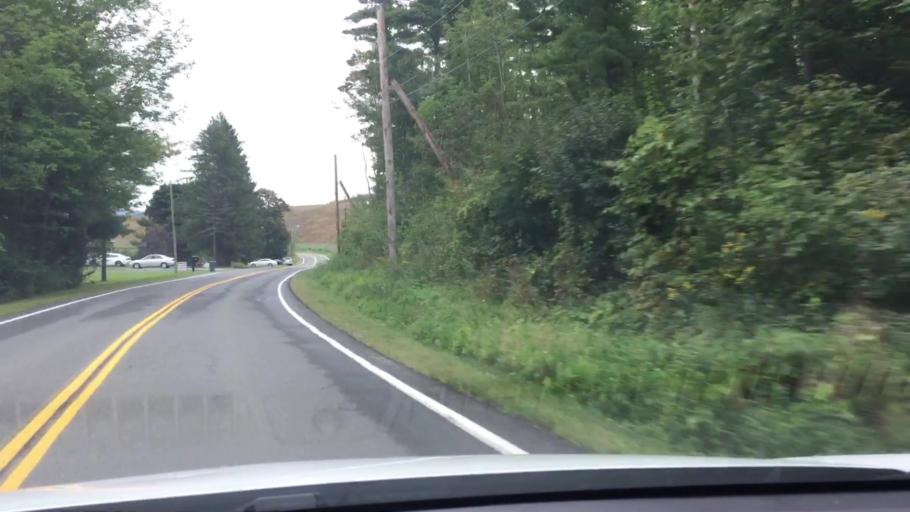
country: US
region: Massachusetts
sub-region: Berkshire County
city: Pittsfield
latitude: 42.4322
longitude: -73.2871
